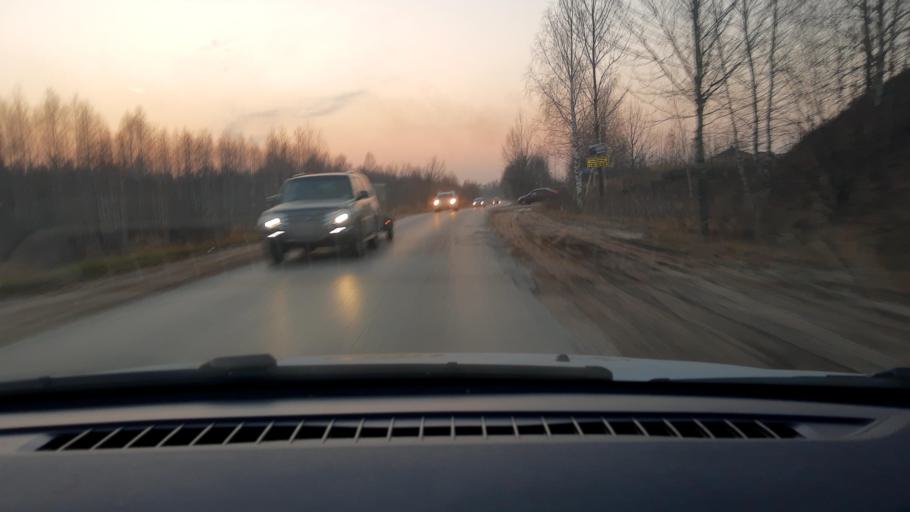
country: RU
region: Nizjnij Novgorod
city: Neklyudovo
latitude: 56.4214
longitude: 43.9458
